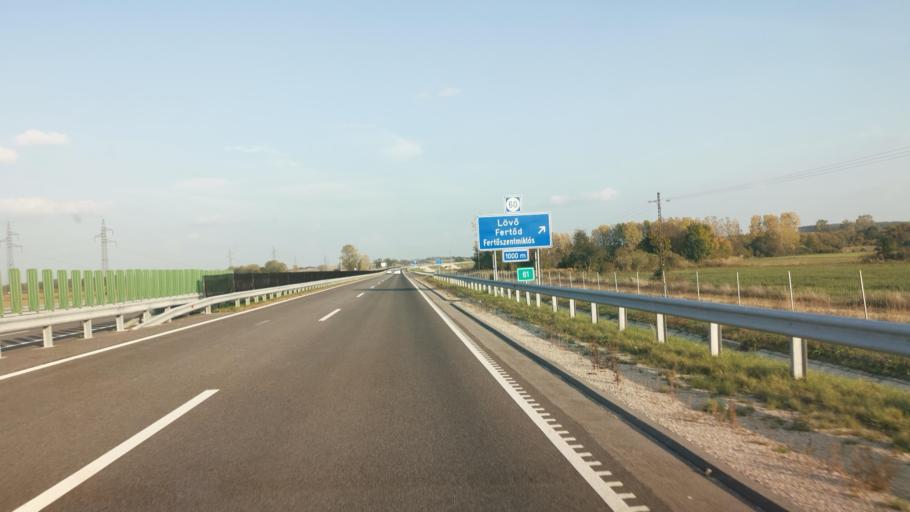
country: HU
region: Gyor-Moson-Sopron
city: Fertoszentmiklos
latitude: 47.5693
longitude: 16.8425
